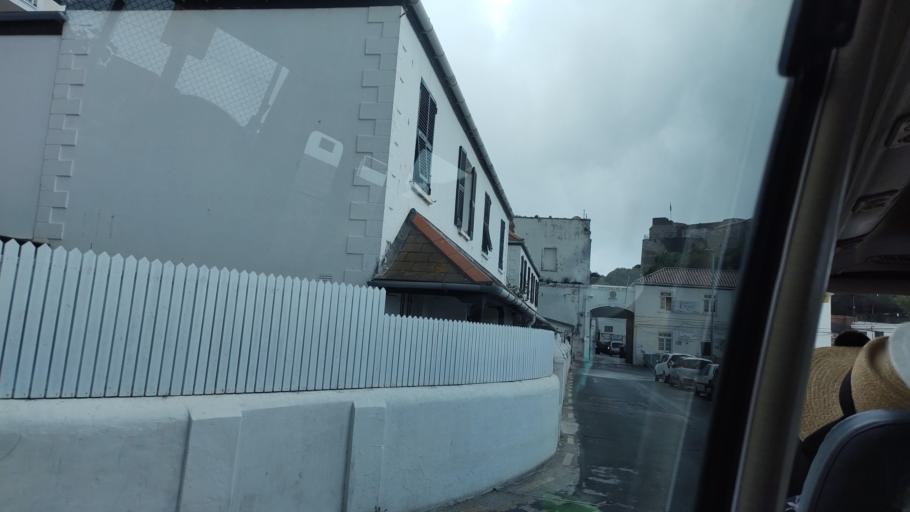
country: GI
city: Gibraltar
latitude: 36.1213
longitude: -5.3522
